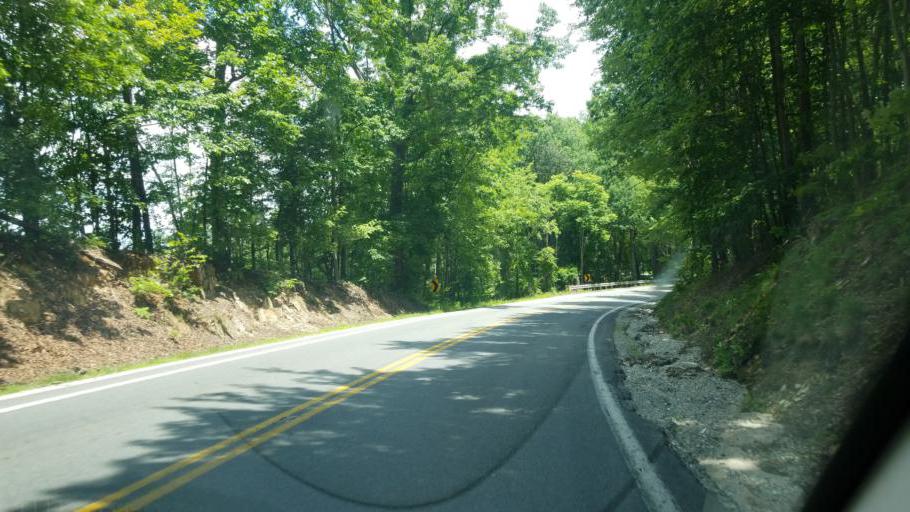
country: US
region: Virginia
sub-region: Amherst County
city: Amherst
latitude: 37.5670
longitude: -78.9389
